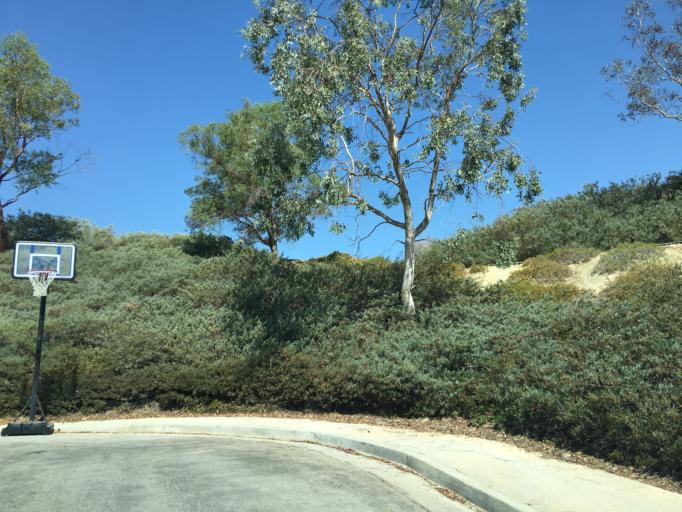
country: US
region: California
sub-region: Los Angeles County
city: Castaic
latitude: 34.4741
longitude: -118.6310
